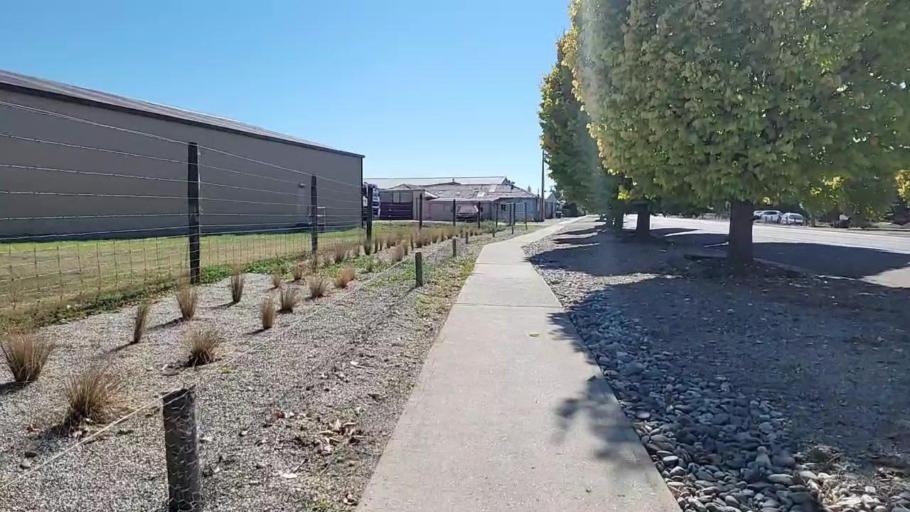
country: NZ
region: Otago
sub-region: Queenstown-Lakes District
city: Wanaka
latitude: -45.0983
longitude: 169.5977
